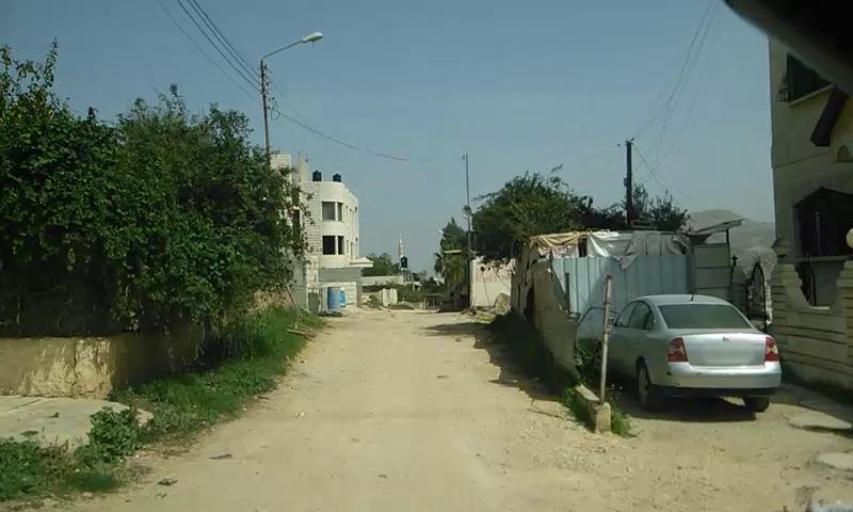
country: PS
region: West Bank
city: `Azmut
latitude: 32.2243
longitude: 35.2974
